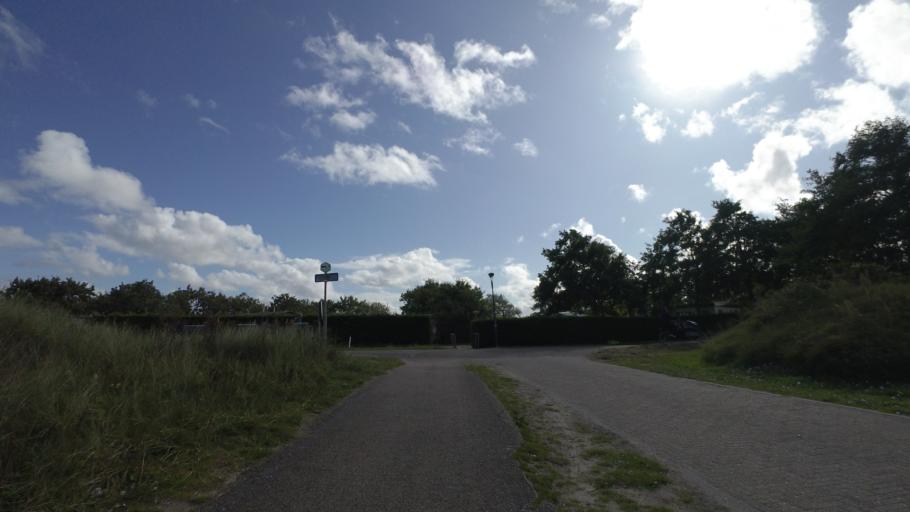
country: NL
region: Friesland
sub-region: Gemeente Ameland
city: Nes
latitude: 53.4539
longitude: 5.8142
